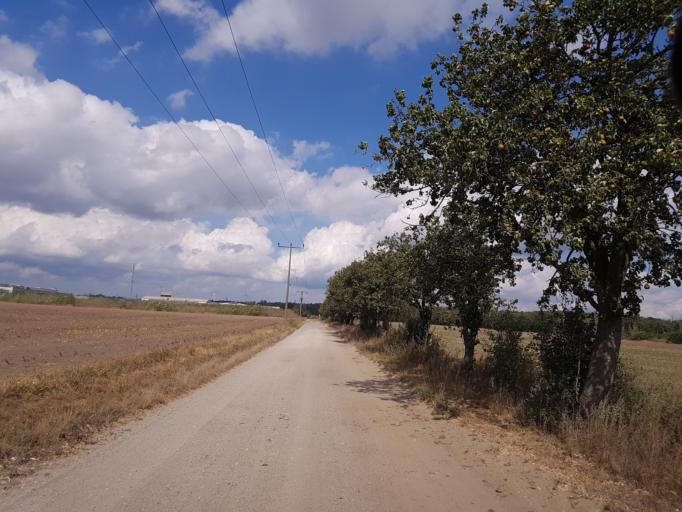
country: DE
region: Brandenburg
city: Finsterwalde
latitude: 51.6296
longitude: 13.7522
